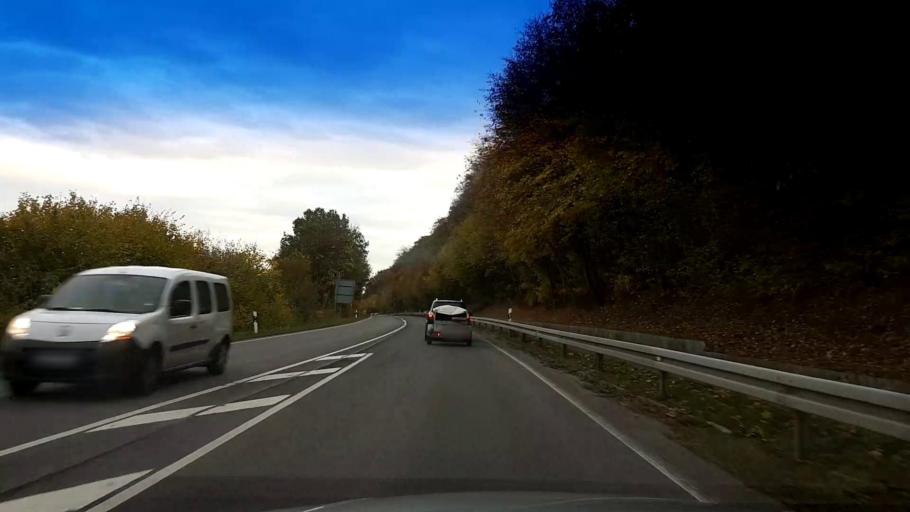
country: DE
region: Bavaria
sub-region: Regierungsbezirk Unterfranken
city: Stettfeld
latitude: 49.9545
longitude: 10.7166
